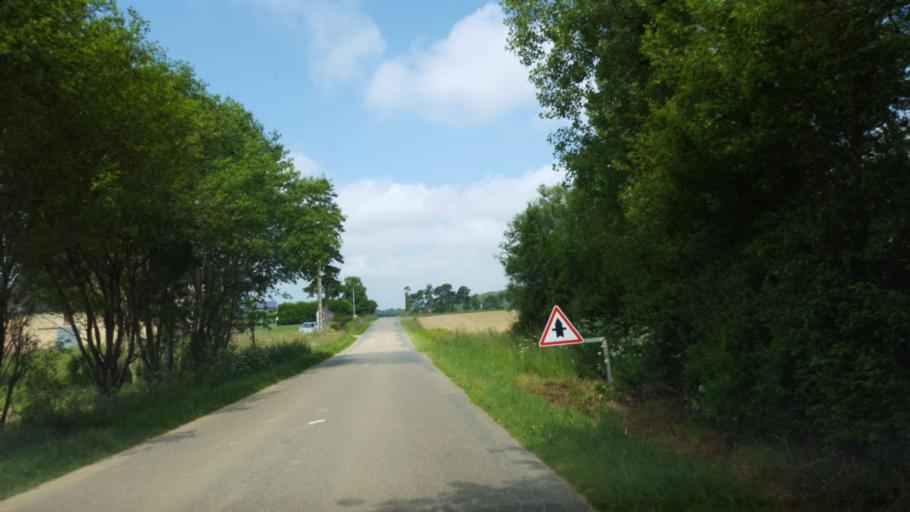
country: FR
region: Brittany
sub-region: Departement d'Ille-et-Vilaine
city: Guignen
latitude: 47.9227
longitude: -1.8809
